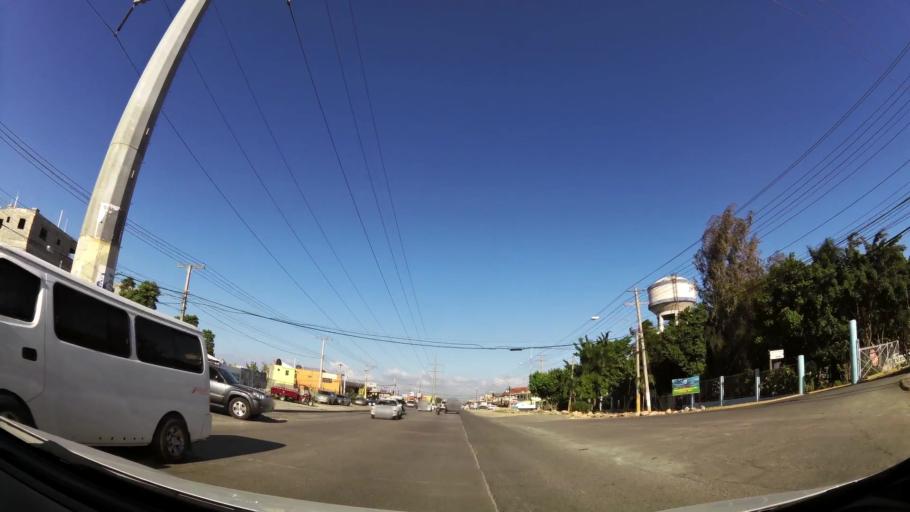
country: DO
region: Santo Domingo
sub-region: Santo Domingo
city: Santo Domingo Este
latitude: 18.4926
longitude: -69.8129
